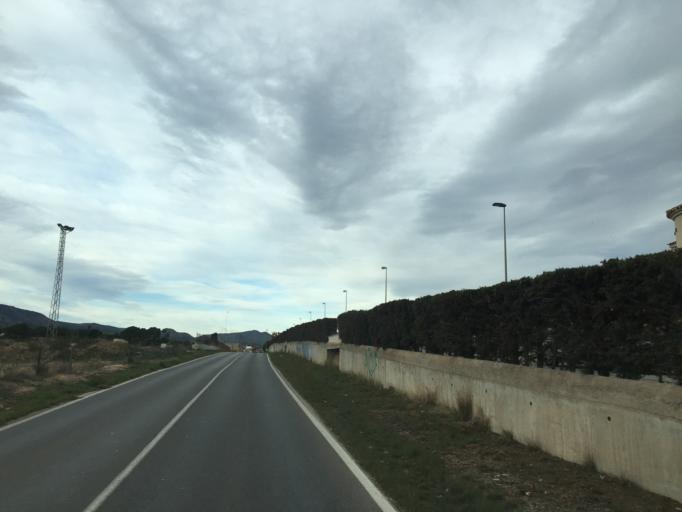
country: ES
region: Murcia
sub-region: Murcia
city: Cartagena
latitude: 37.6117
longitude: -1.0283
